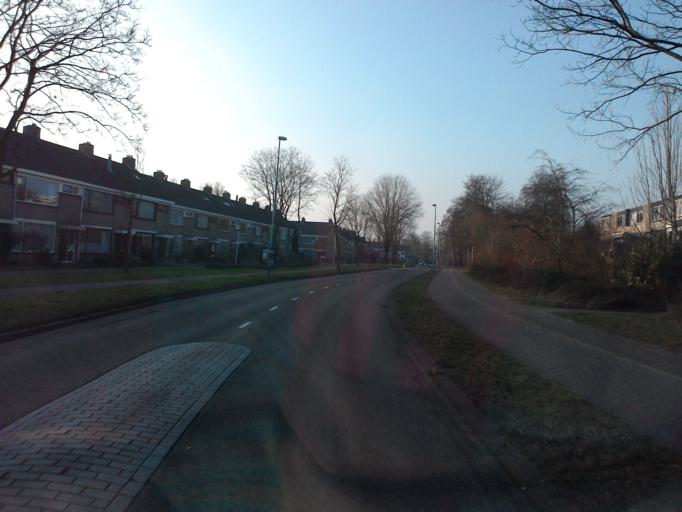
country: NL
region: Utrecht
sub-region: Gemeente Zeist
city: Zeist
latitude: 52.0774
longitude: 5.2233
